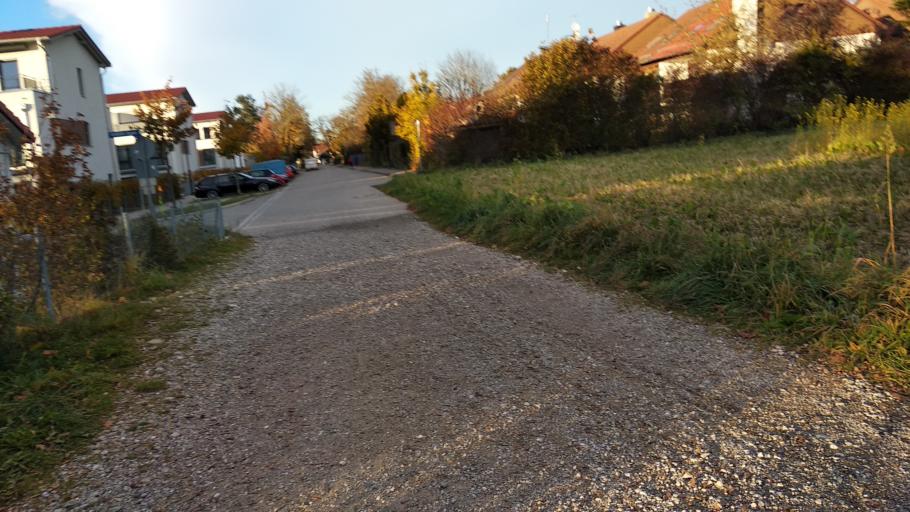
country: DE
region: Bavaria
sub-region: Upper Bavaria
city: Hohenkirchen-Siegertsbrunn
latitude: 48.0179
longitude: 11.7225
